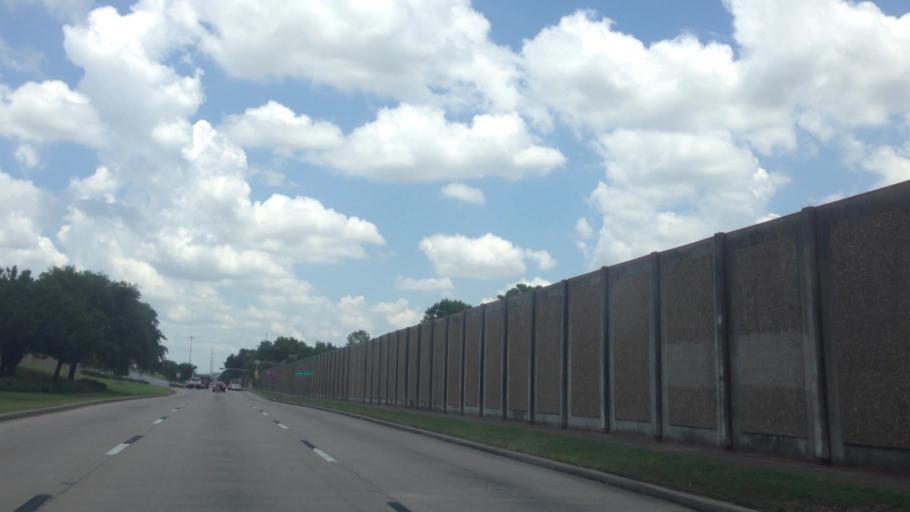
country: US
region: Texas
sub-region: Harris County
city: Bunker Hill Village
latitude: 29.7451
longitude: -95.5572
